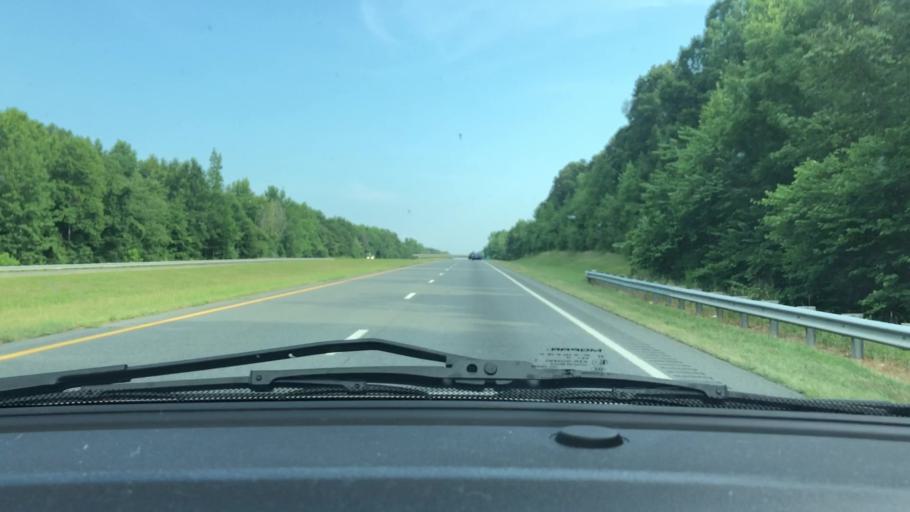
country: US
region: North Carolina
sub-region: Guilford County
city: Forest Oaks
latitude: 35.9403
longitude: -79.6866
